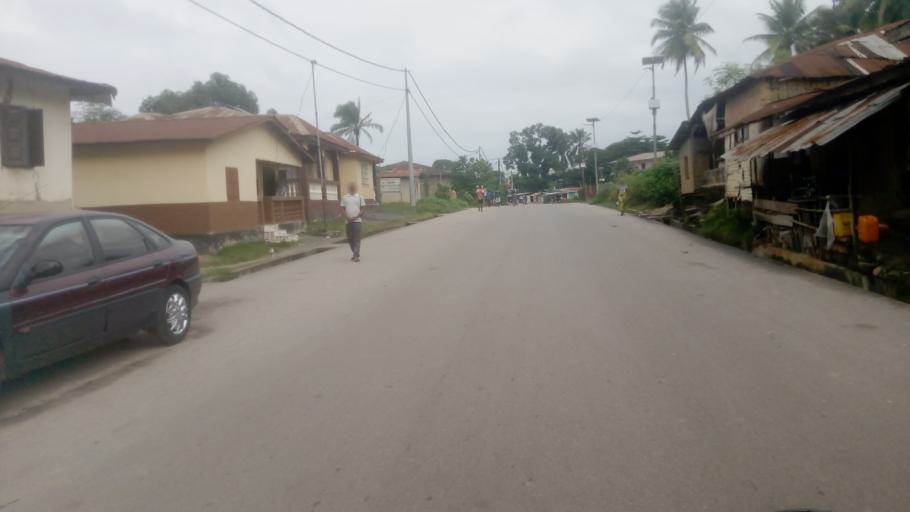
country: SL
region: Northern Province
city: Lunsar
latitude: 8.6871
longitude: -12.5352
